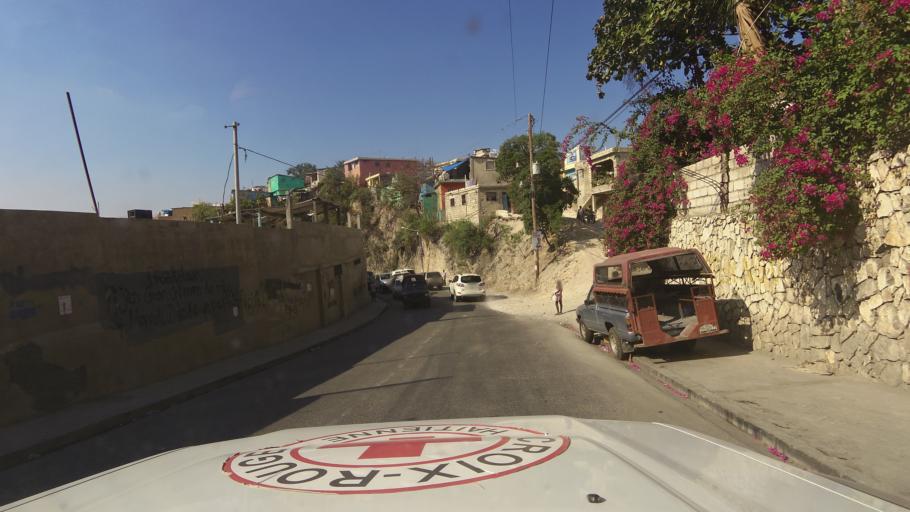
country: HT
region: Ouest
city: Petionville
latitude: 18.5153
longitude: -72.2784
